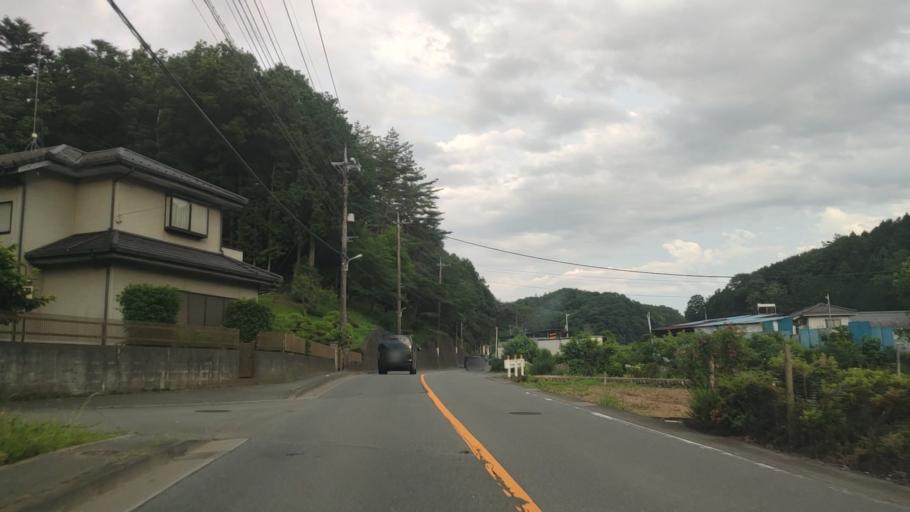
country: JP
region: Saitama
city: Hanno
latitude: 35.8188
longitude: 139.2947
